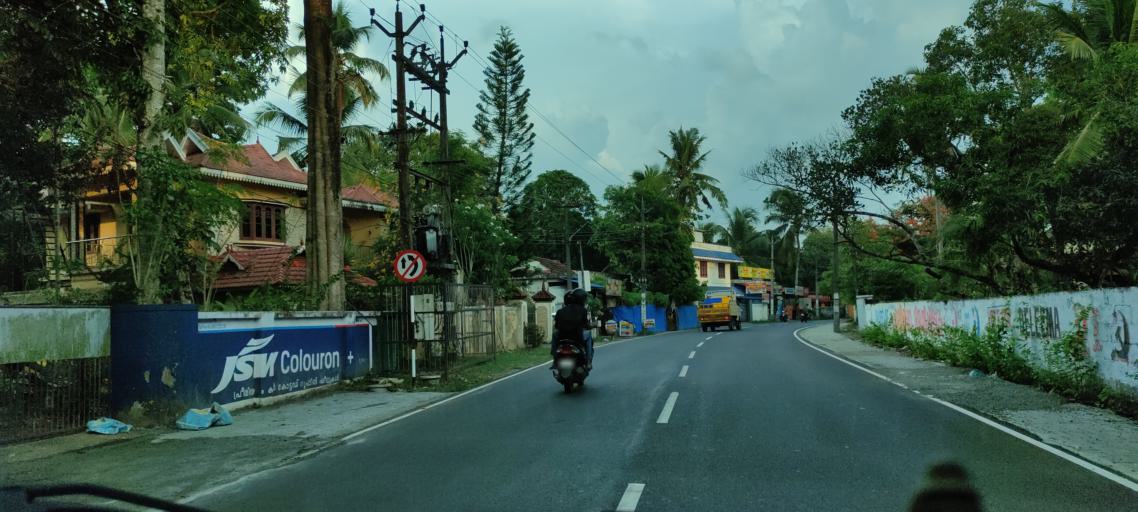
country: IN
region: Kerala
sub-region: Alappuzha
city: Arukutti
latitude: 9.8371
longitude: 76.3323
